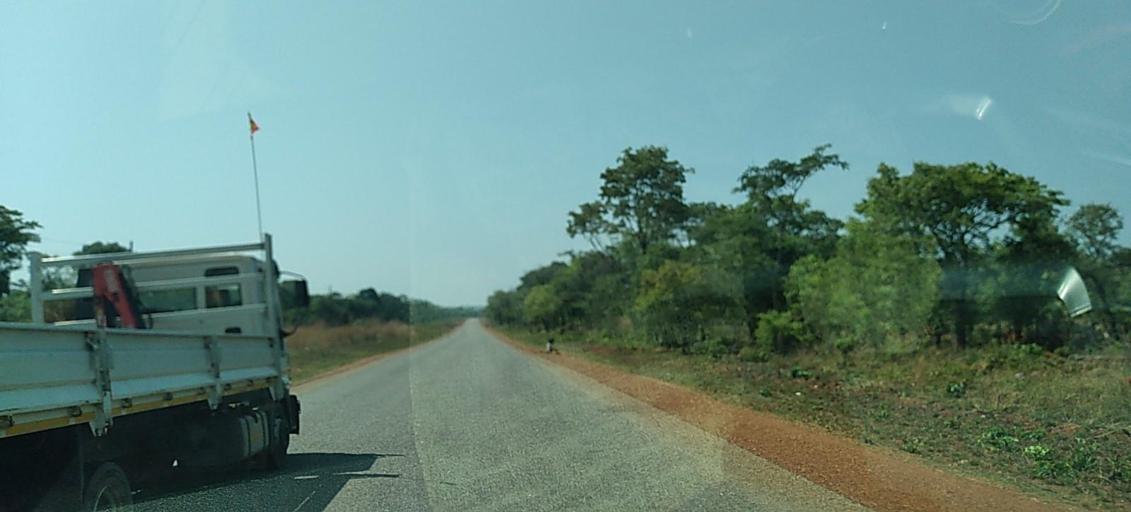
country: ZM
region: North-Western
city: Solwezi
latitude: -12.2124
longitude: 25.5601
